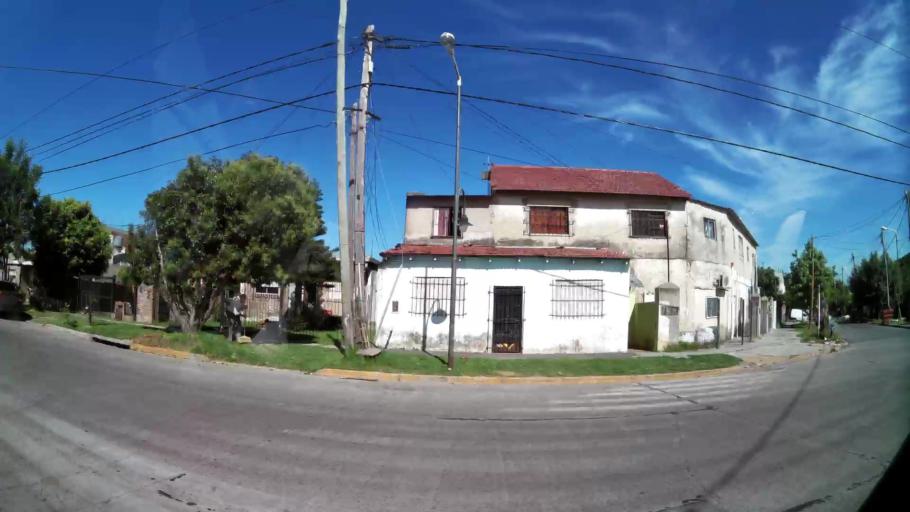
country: AR
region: Buenos Aires
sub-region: Partido de Tigre
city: Tigre
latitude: -34.4764
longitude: -58.5798
